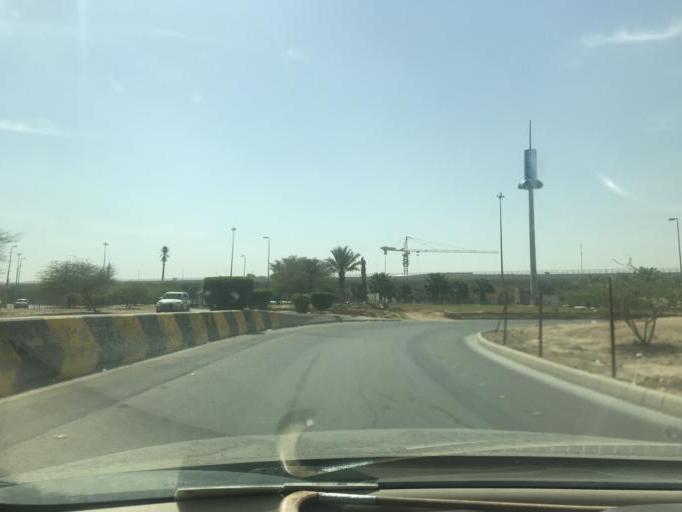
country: SA
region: Ar Riyad
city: Riyadh
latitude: 24.8220
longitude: 46.7186
